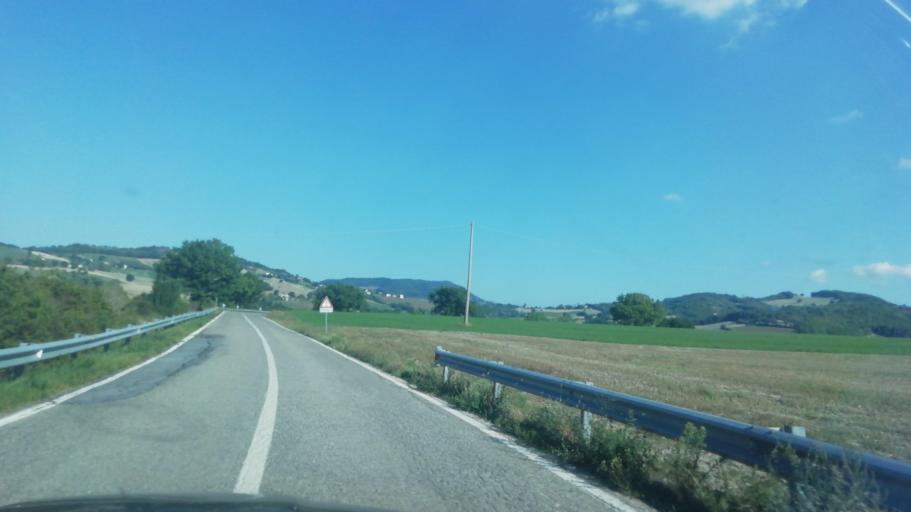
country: IT
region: The Marches
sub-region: Provincia di Pesaro e Urbino
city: Frontone
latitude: 43.5415
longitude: 12.7069
